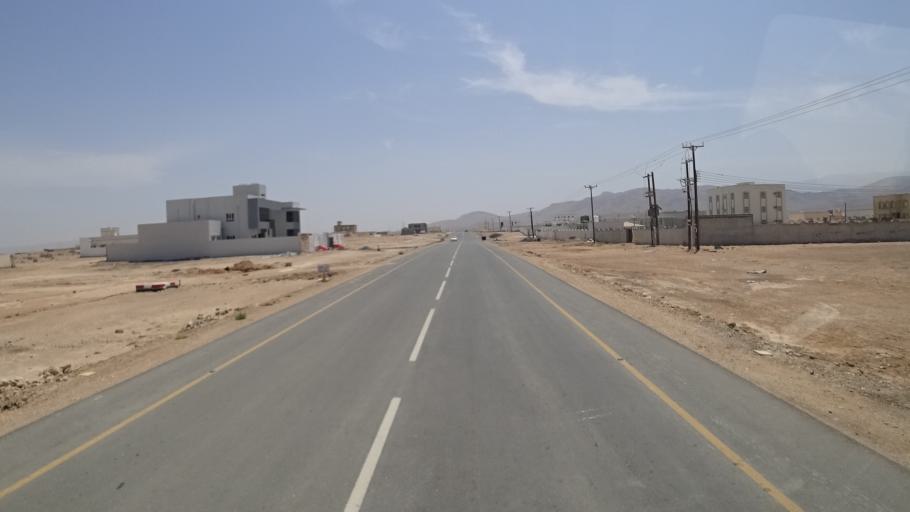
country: OM
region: Ash Sharqiyah
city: Sur
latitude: 22.5975
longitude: 59.4617
